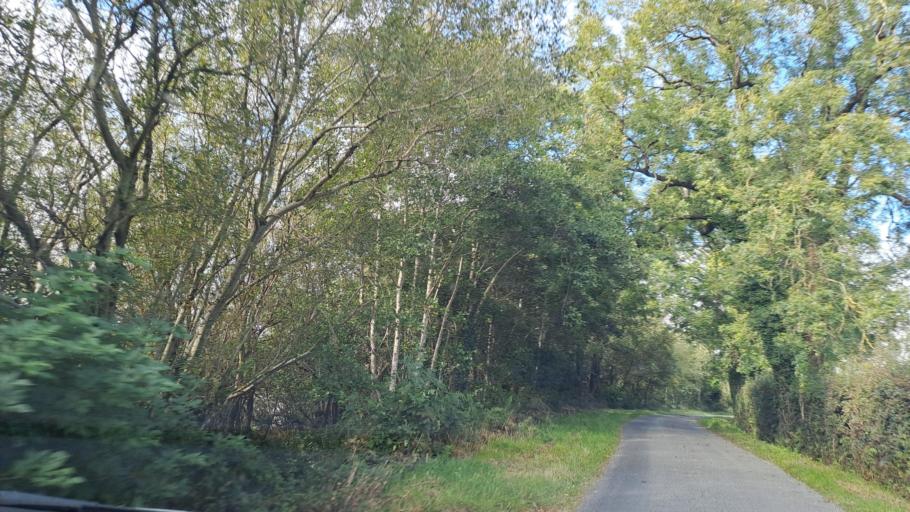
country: IE
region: Ulster
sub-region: An Cabhan
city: Kingscourt
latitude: 53.9718
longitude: -6.8617
